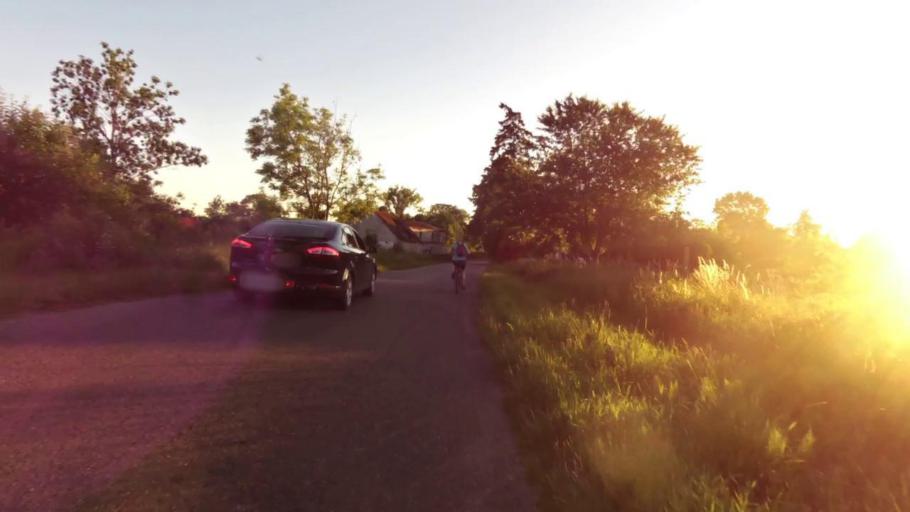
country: PL
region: West Pomeranian Voivodeship
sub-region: Powiat bialogardzki
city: Bialogard
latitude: 54.0520
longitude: 16.0638
